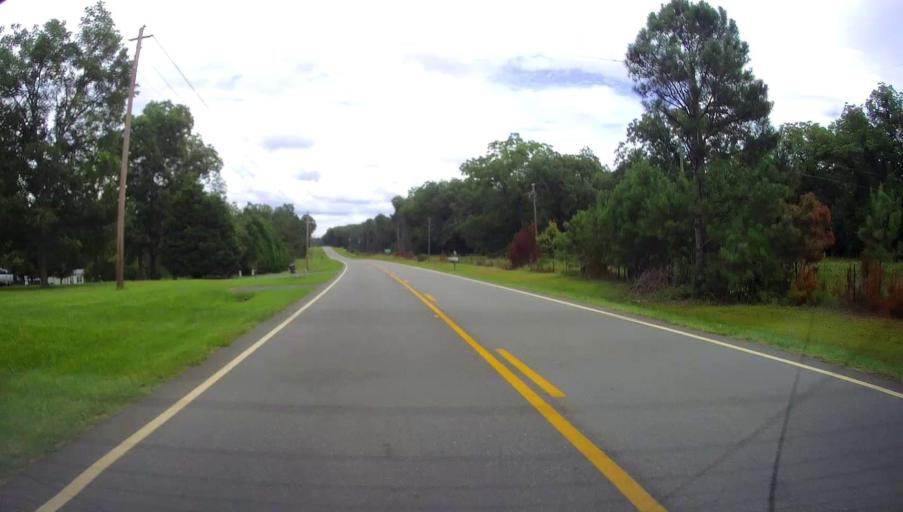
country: US
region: Georgia
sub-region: Schley County
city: Ellaville
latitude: 32.2569
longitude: -84.2677
